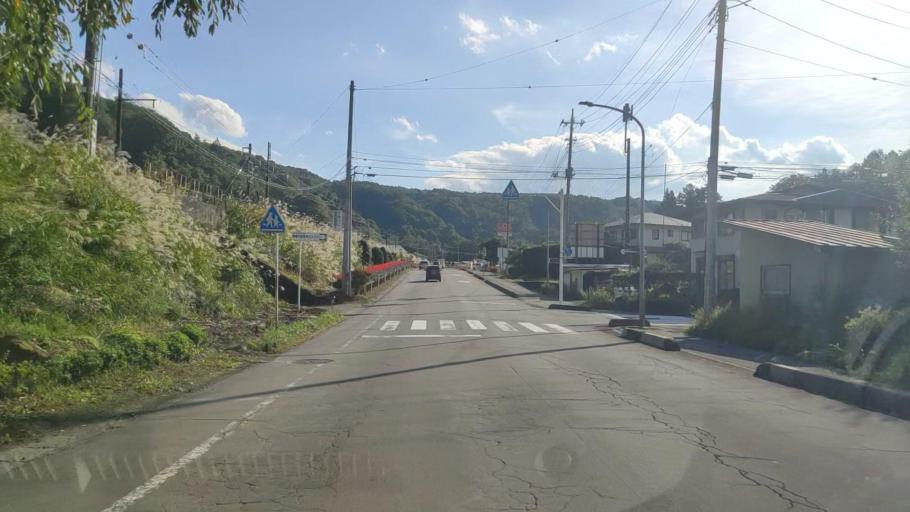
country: JP
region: Nagano
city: Komoro
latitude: 36.5232
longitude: 138.5424
